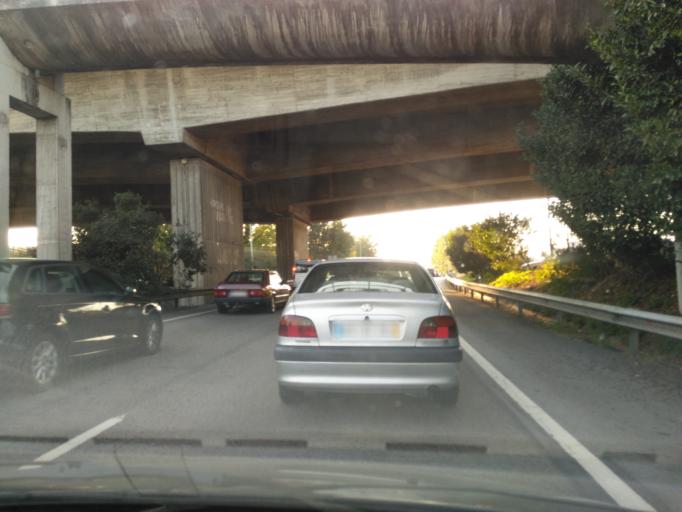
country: PT
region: Braga
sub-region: Guimaraes
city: Candoso
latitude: 41.4396
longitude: -8.3295
